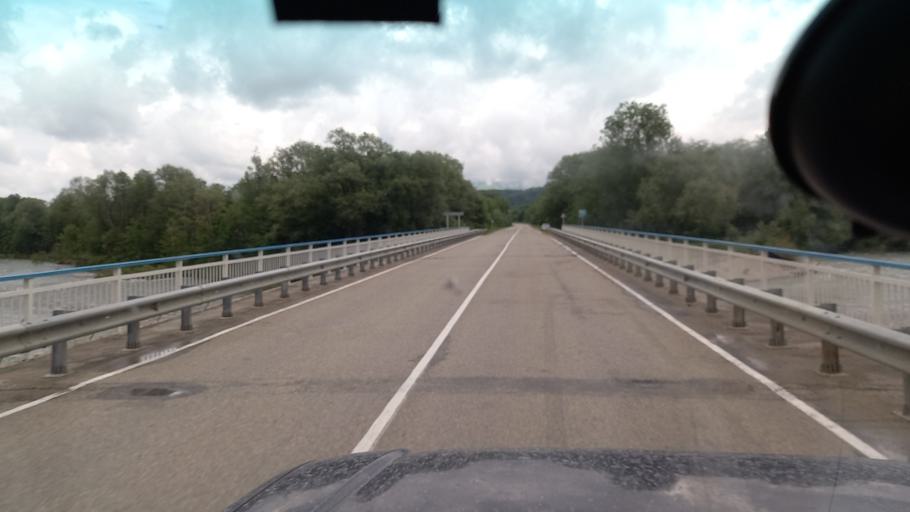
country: RU
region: Krasnodarskiy
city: Psebay
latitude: 44.0886
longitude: 40.7910
